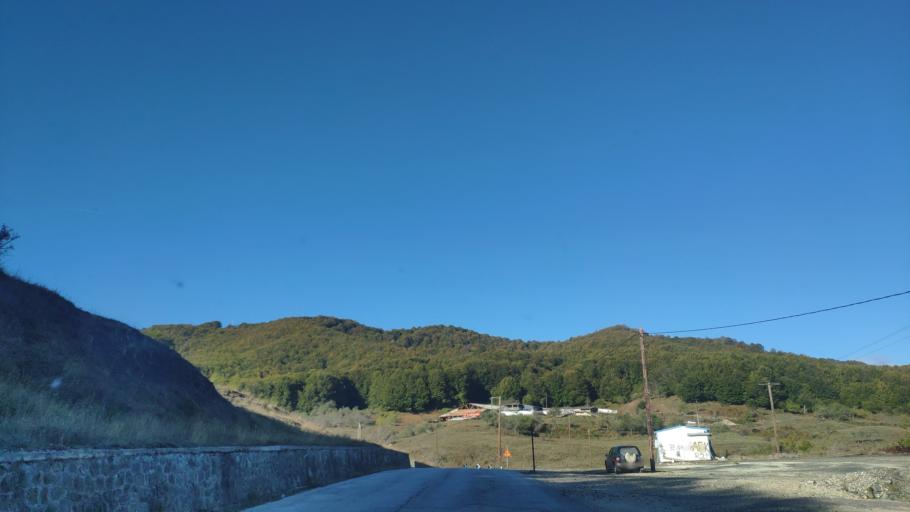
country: GR
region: Epirus
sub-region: Nomos Ioanninon
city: Metsovo
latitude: 39.7793
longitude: 21.1647
